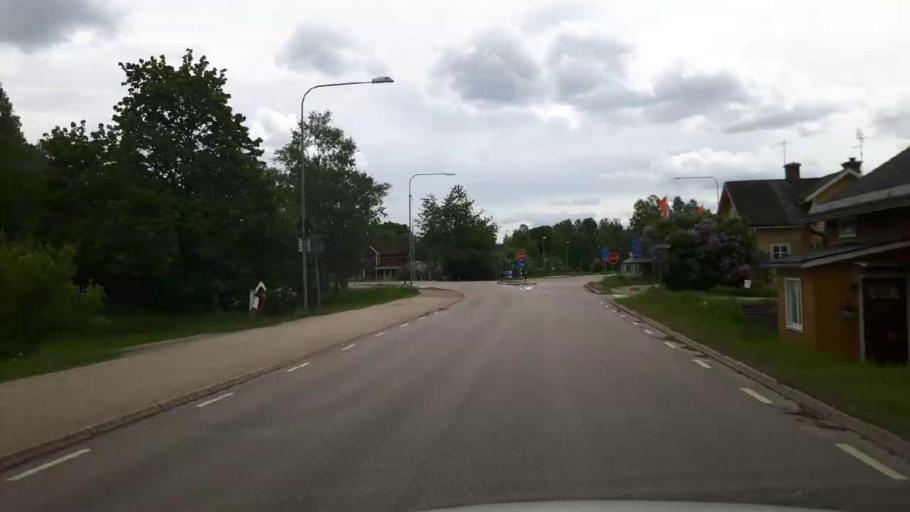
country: SE
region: Vaestmanland
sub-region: Norbergs Kommun
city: Norberg
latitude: 60.0752
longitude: 15.9300
